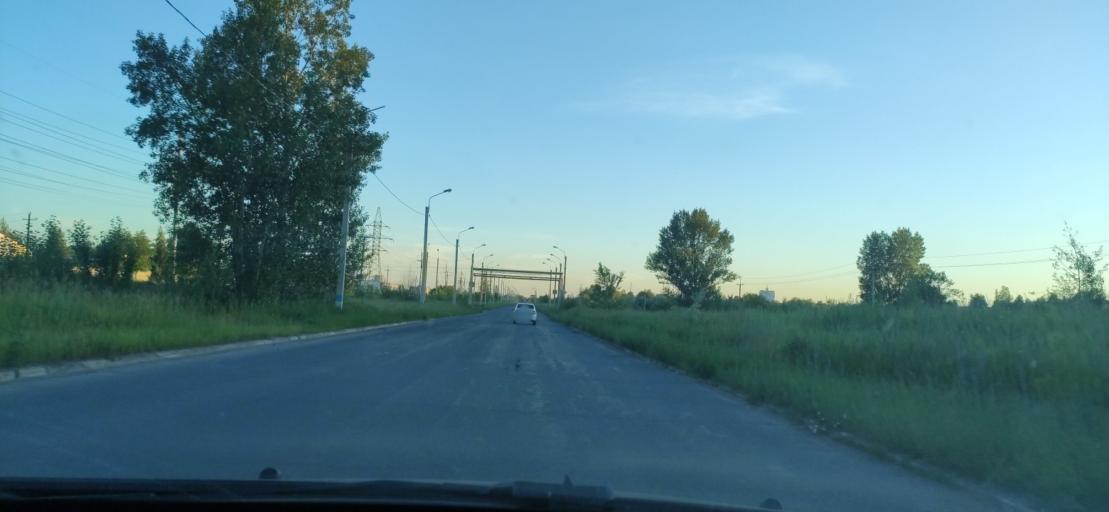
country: RU
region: Ulyanovsk
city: Mirnyy
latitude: 54.3747
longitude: 48.6534
